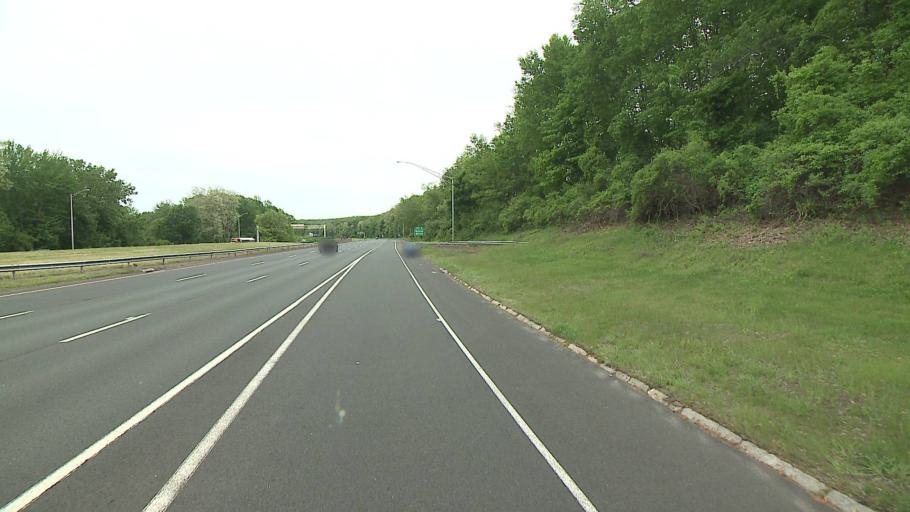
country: US
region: Connecticut
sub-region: Hartford County
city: Manchester
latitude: 41.7617
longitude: -72.5153
